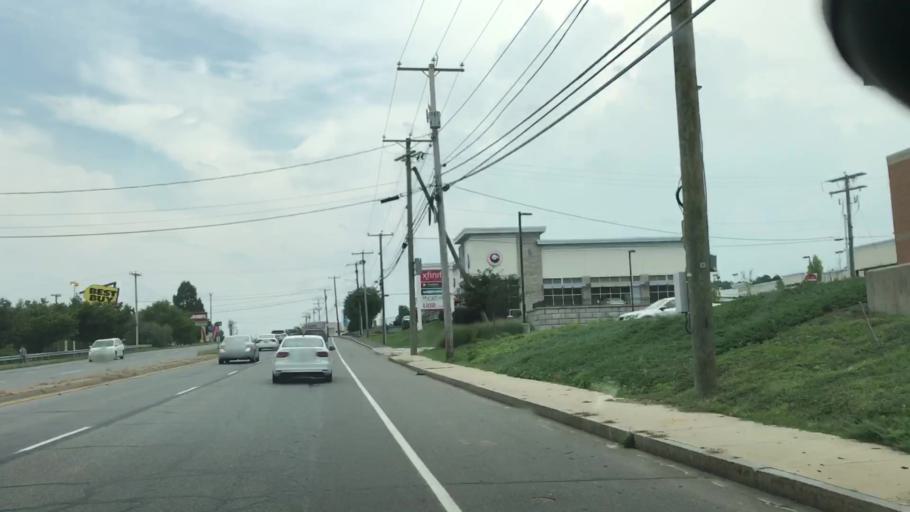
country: US
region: Massachusetts
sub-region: Middlesex County
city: Tyngsboro
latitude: 42.7139
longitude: -71.4427
